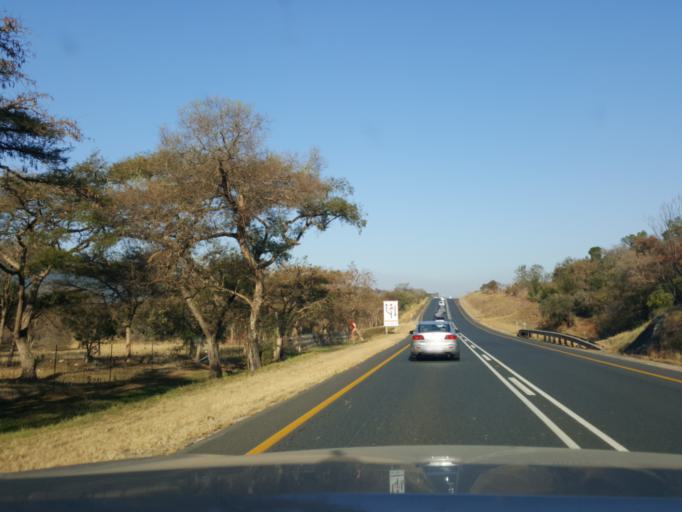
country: ZA
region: Mpumalanga
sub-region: Ehlanzeni District
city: Lydenburg
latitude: -25.3998
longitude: 30.6146
